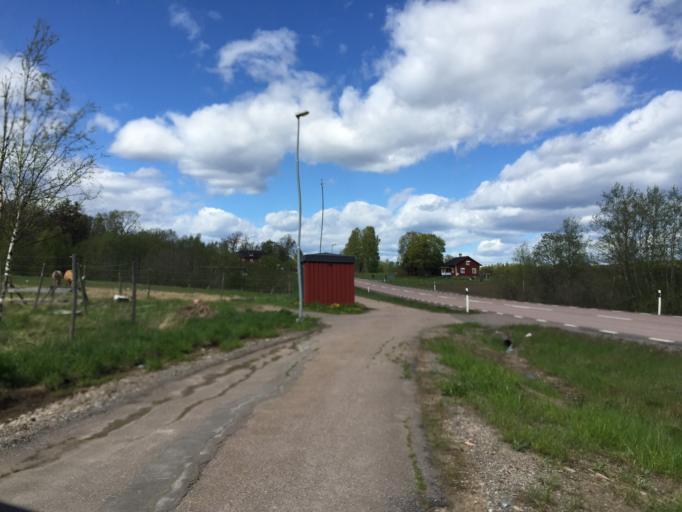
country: SE
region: Dalarna
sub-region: Ludvika Kommun
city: Ludvika
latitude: 60.1941
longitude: 15.2141
